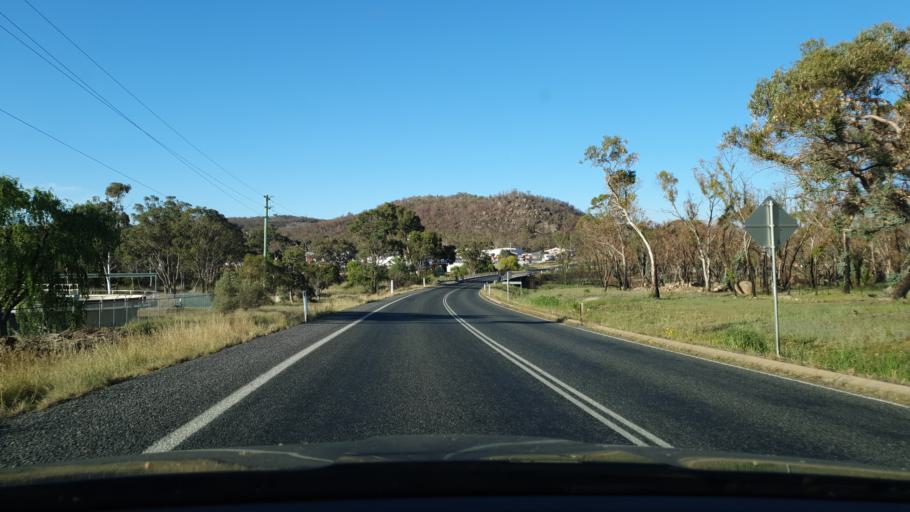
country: AU
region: Queensland
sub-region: Southern Downs
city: Stanthorpe
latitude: -28.6550
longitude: 151.9175
